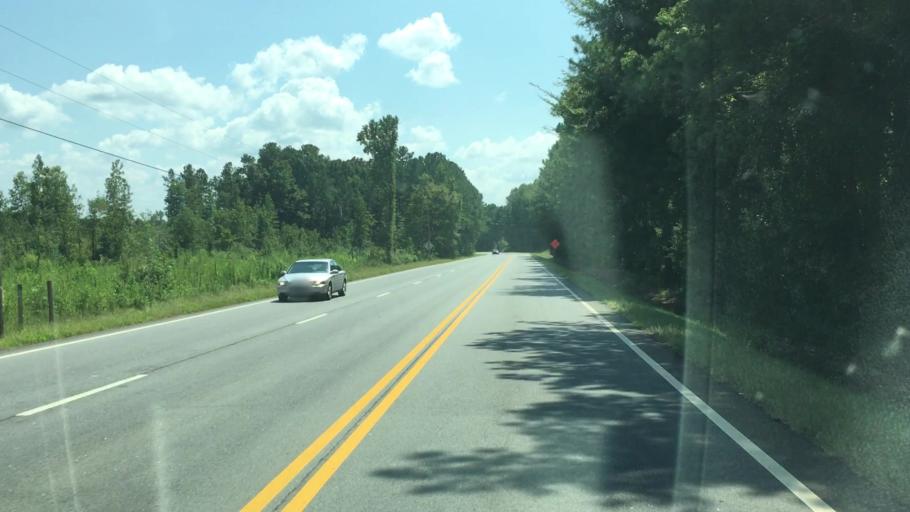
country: US
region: Georgia
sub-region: Oconee County
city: Watkinsville
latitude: 33.7344
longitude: -83.4298
